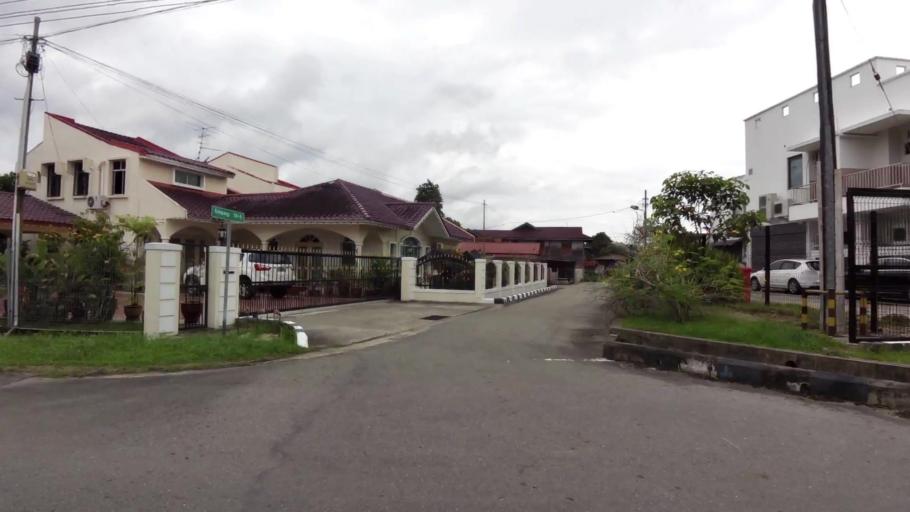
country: BN
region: Brunei and Muara
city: Bandar Seri Begawan
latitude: 4.8971
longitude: 114.9161
